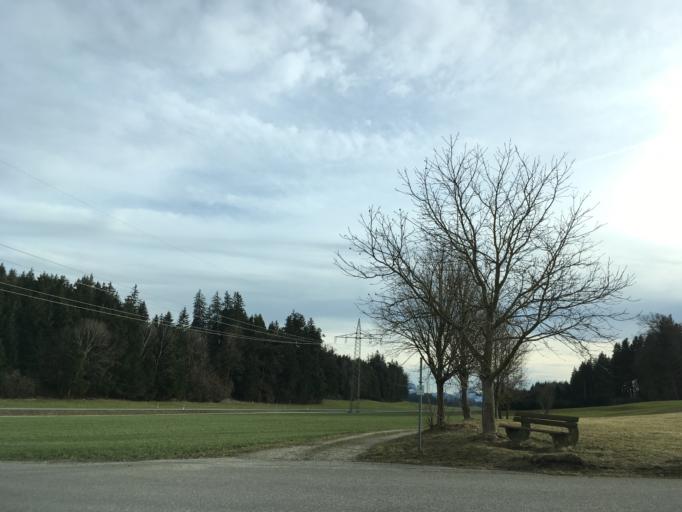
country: DE
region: Bavaria
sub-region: Upper Bavaria
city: Sochtenau
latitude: 47.9287
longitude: 12.2211
